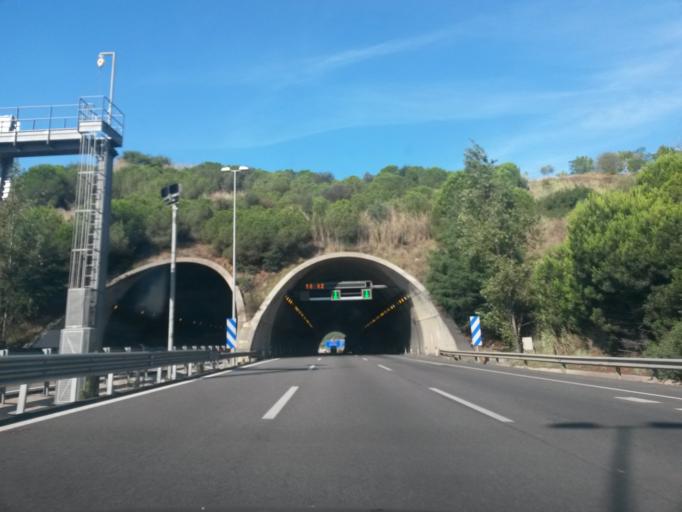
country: ES
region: Catalonia
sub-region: Provincia de Barcelona
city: Mataro
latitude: 41.5514
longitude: 2.4283
